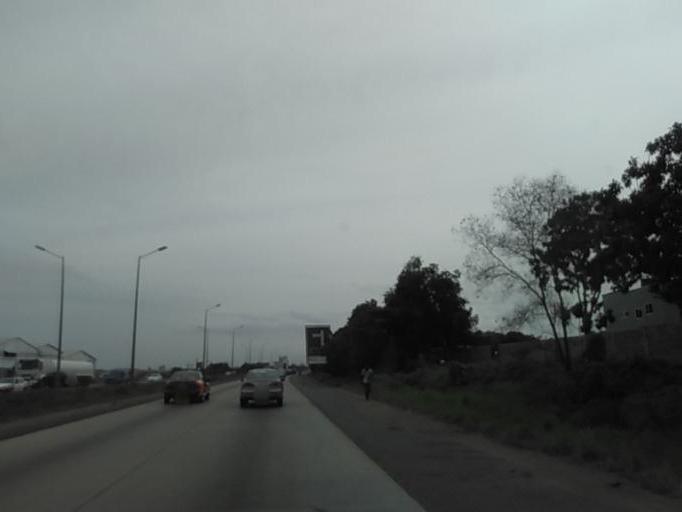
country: GH
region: Greater Accra
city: Medina Estates
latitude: 5.6313
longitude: -0.1518
